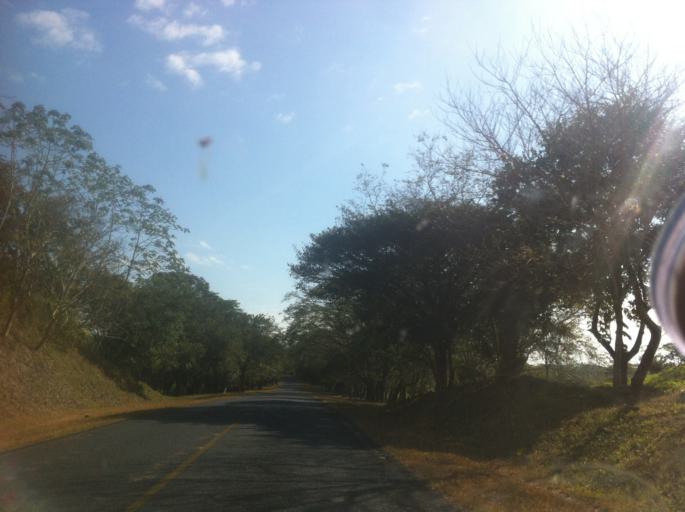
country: NI
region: Rio San Juan
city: San Miguelito
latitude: 11.4347
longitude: -84.8659
